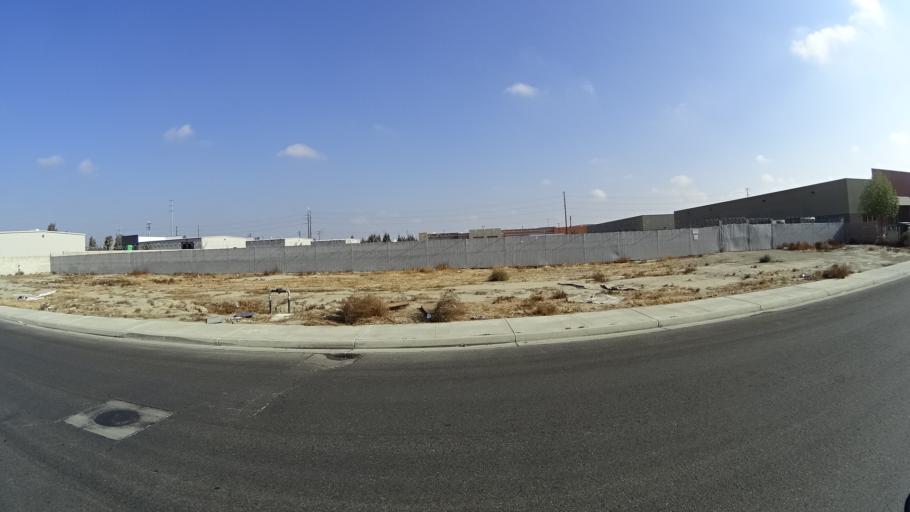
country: US
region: California
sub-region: Kern County
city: Greenacres
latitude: 35.3094
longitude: -119.0988
